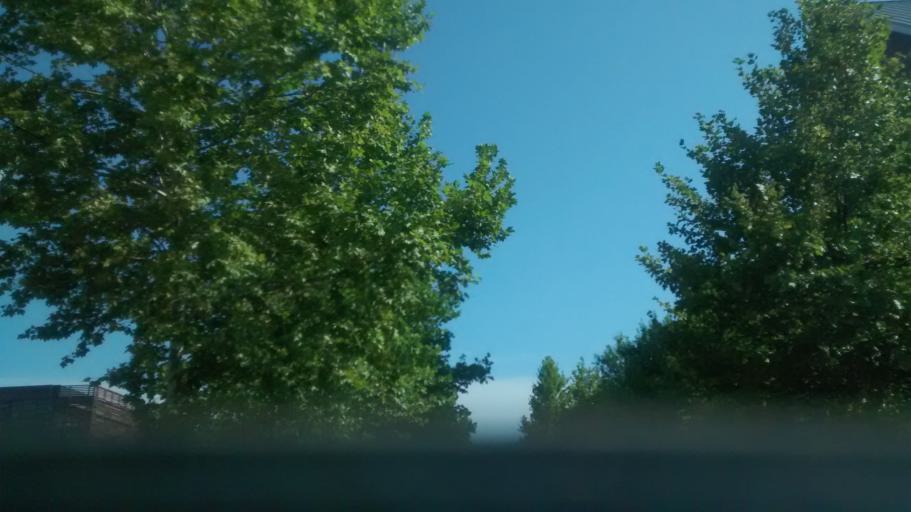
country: US
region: Arkansas
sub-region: Washington County
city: Fayetteville
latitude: 36.0728
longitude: -94.1755
